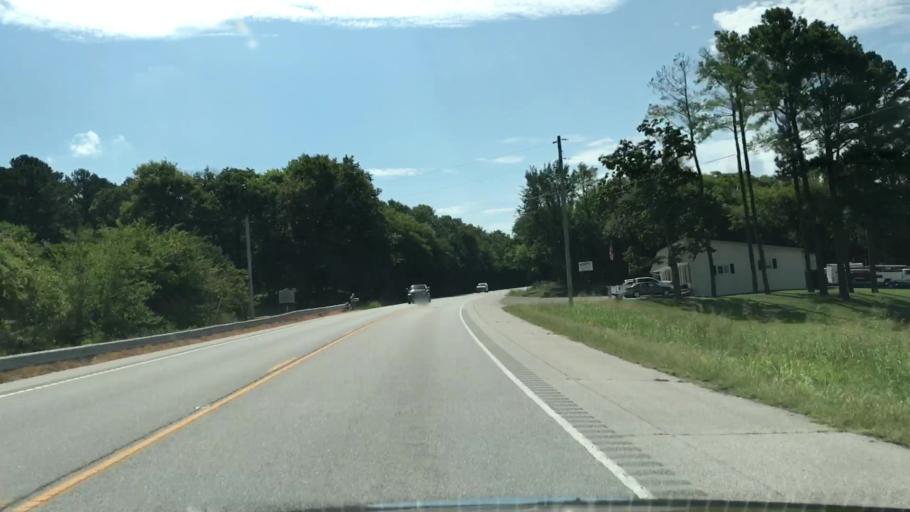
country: US
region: Tennessee
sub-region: Smith County
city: Carthage
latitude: 36.3321
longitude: -86.0239
